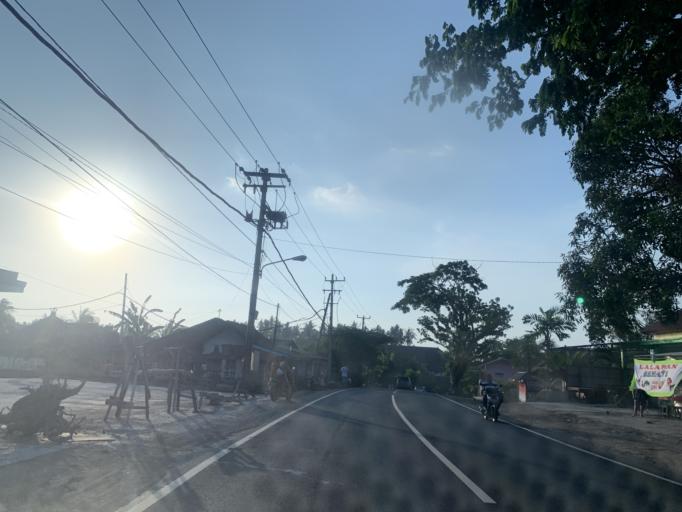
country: ID
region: Bali
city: Banjar Delodrurung
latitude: -8.4944
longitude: 114.9633
